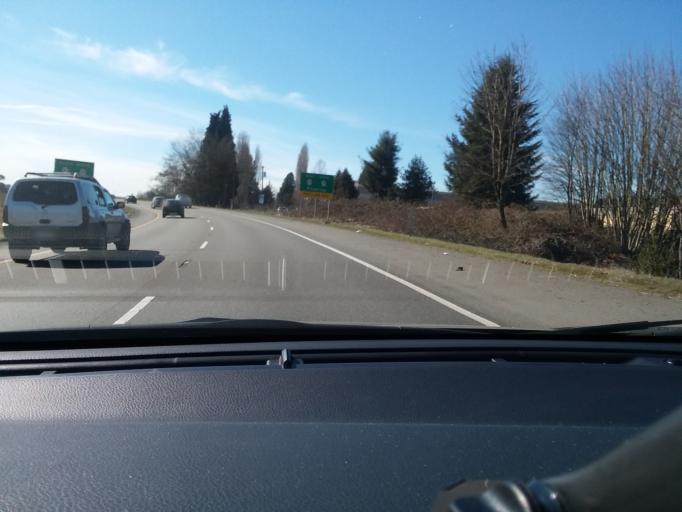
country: US
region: Washington
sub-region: Pierce County
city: Sumner
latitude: 47.2028
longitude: -122.2587
